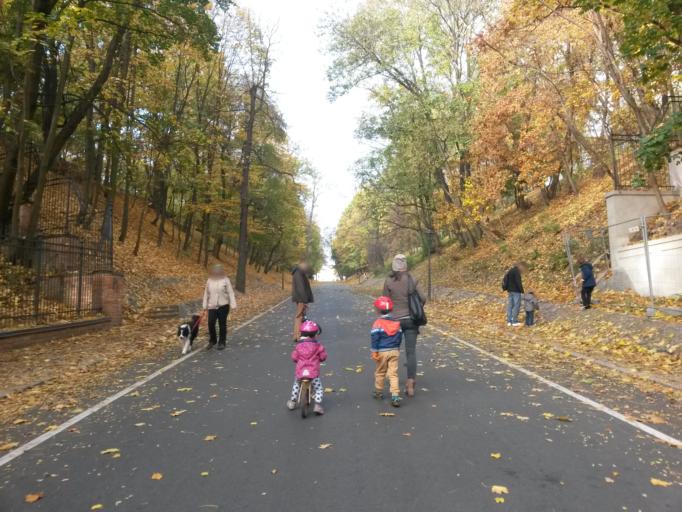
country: PL
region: Masovian Voivodeship
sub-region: Warszawa
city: Srodmiescie
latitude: 52.2180
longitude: 21.0309
